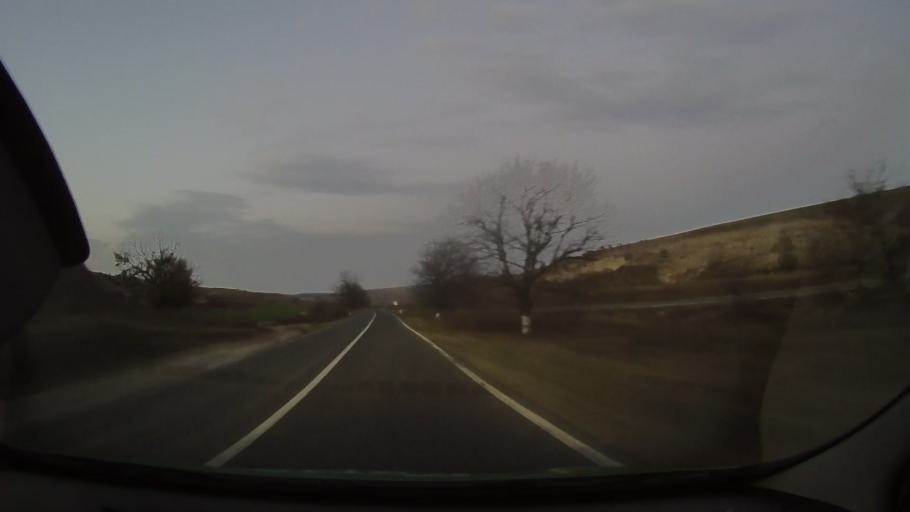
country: RO
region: Constanta
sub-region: Comuna Ion Corvin
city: Ion Corvin
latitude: 44.1049
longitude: 27.7557
